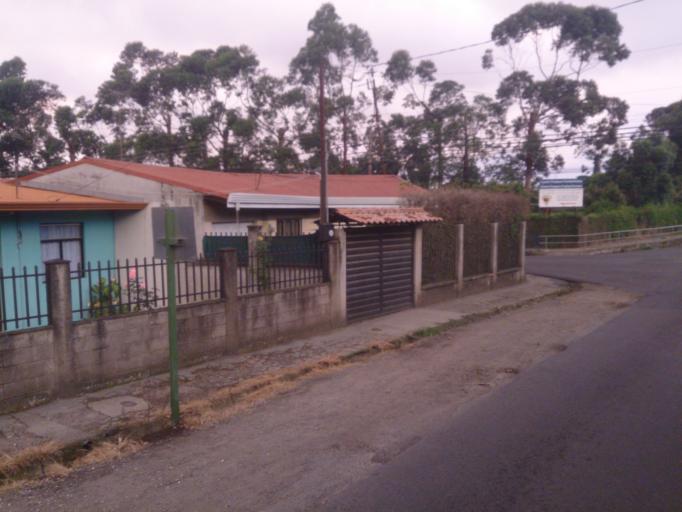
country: CR
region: Cartago
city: Concepcion
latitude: 9.9294
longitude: -84.0040
